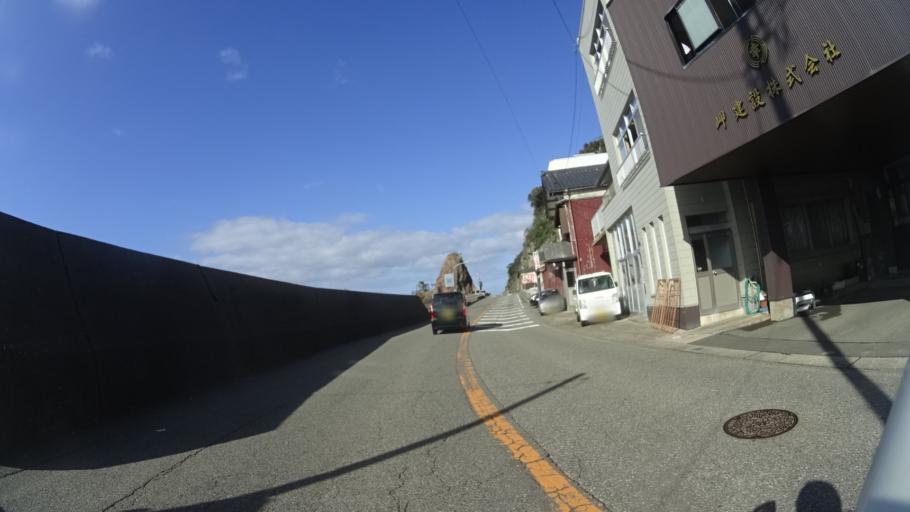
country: JP
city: Asahi
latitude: 35.9558
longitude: 135.9804
